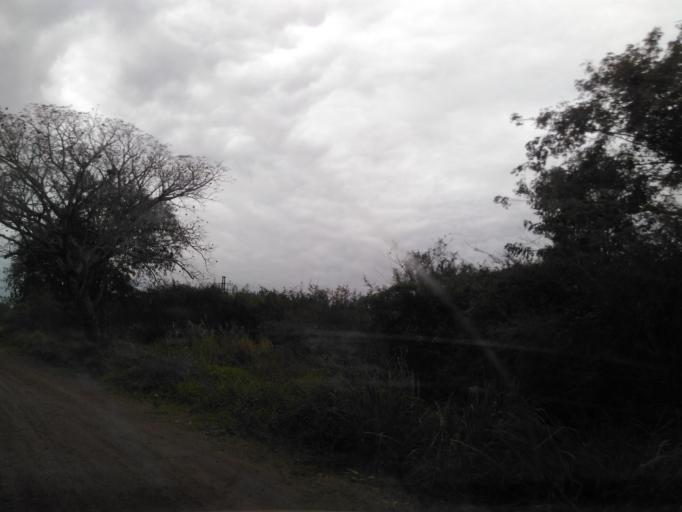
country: AR
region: Chaco
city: Fontana
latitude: -27.4053
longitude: -58.9975
